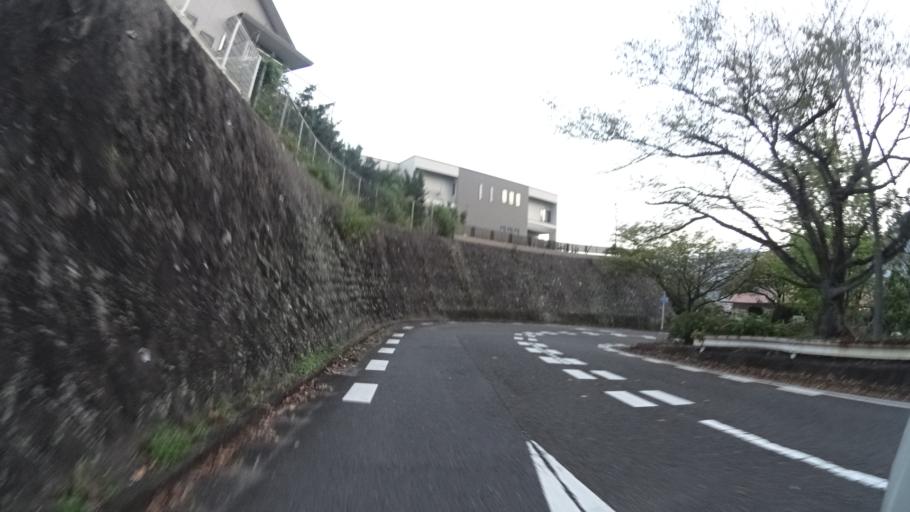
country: JP
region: Oita
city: Beppu
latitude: 33.3143
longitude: 131.4856
